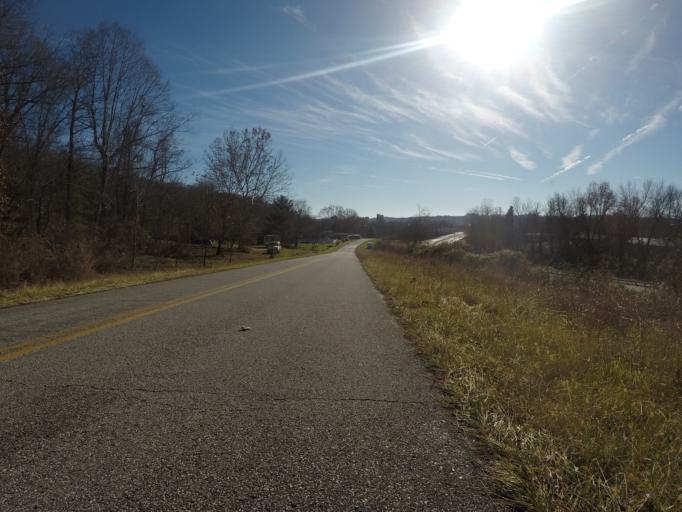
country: US
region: West Virginia
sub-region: Cabell County
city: Huntington
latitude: 38.4337
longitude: -82.4553
